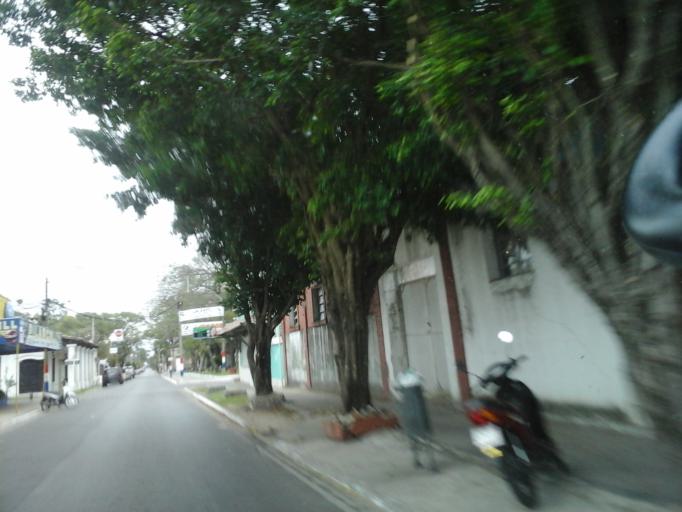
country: PY
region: Neembucu
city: Pilar
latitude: -26.8565
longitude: -58.3042
